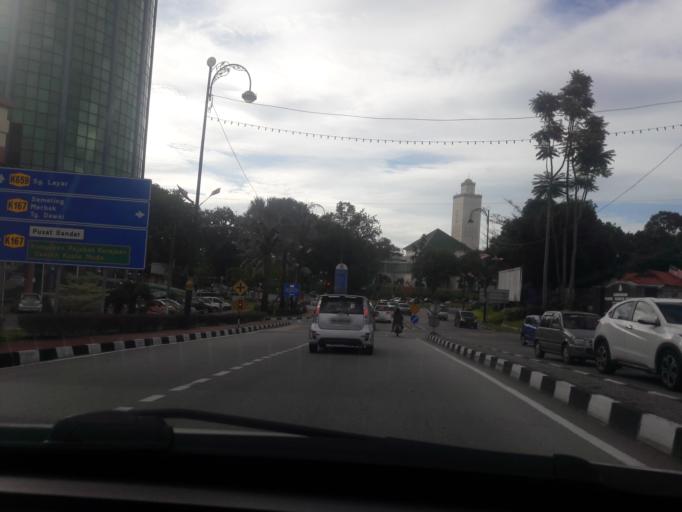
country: MY
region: Kedah
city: Sungai Petani
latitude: 5.6455
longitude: 100.4891
